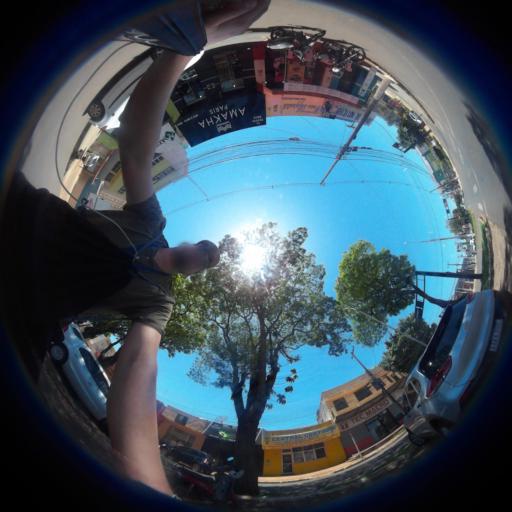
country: BR
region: Mato Grosso do Sul
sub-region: Ponta Pora
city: Ponta Pora
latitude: -22.5425
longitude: -55.7270
